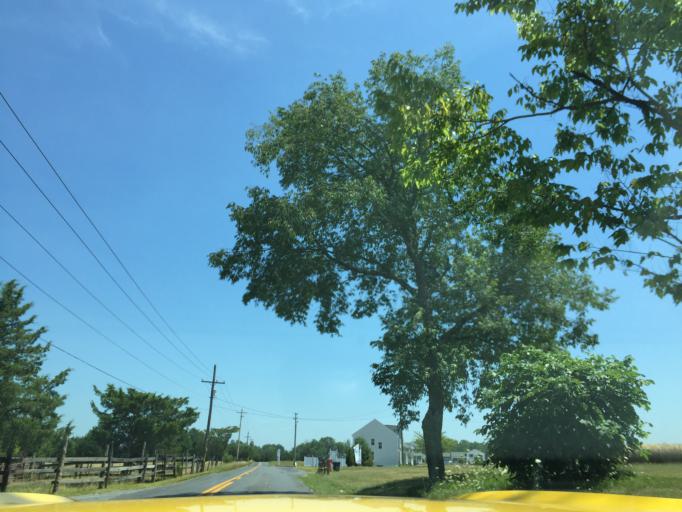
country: US
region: West Virginia
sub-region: Berkeley County
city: Inwood
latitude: 39.3313
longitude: -78.0327
